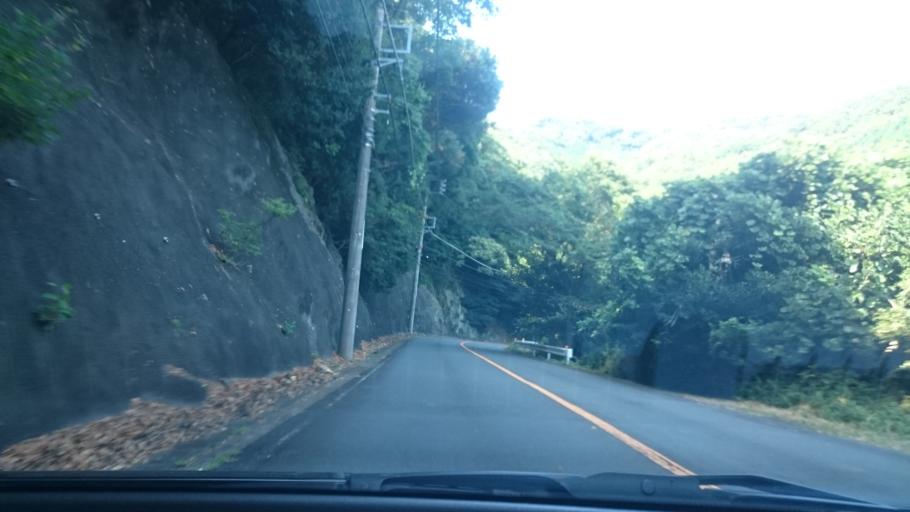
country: JP
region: Shizuoka
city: Heda
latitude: 34.9256
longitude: 138.7841
